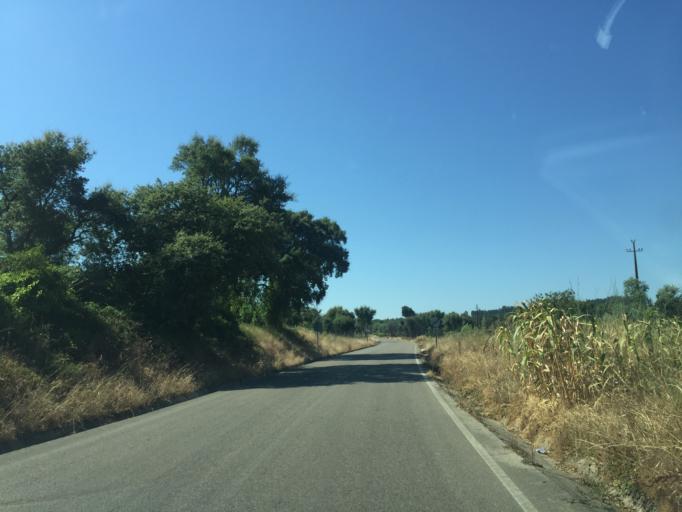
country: PT
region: Santarem
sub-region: Tomar
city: Tomar
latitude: 39.5937
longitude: -8.3284
